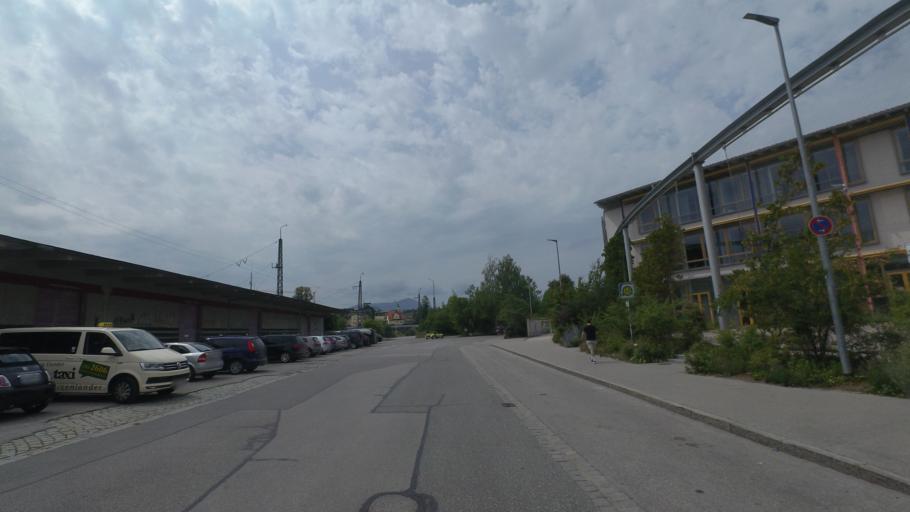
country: DE
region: Bavaria
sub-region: Upper Bavaria
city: Traunstein
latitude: 47.8700
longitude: 12.6382
